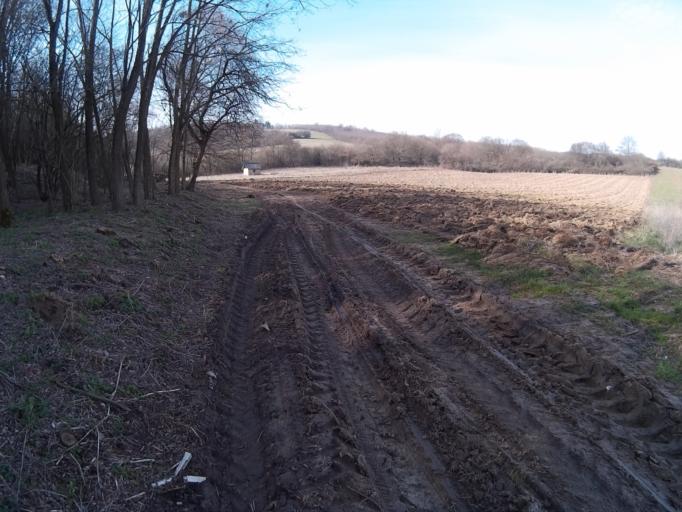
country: HU
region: Nograd
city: Retsag
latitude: 47.8841
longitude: 19.1886
